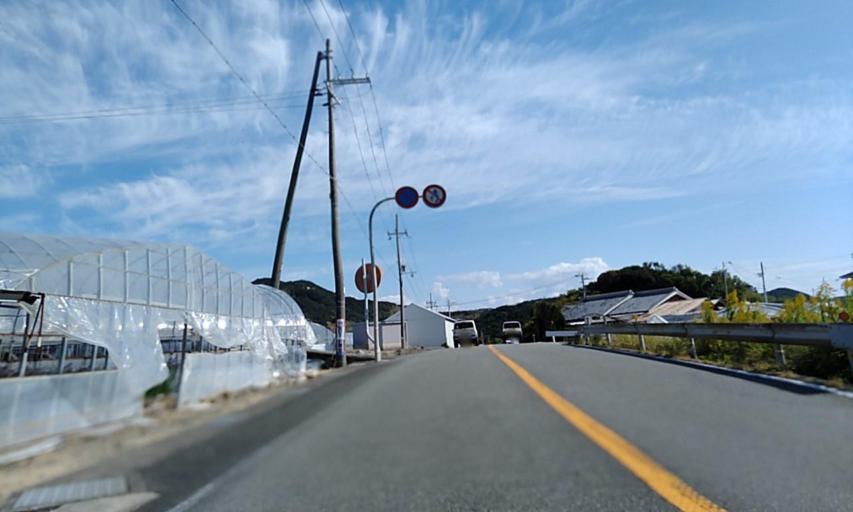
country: JP
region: Wakayama
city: Gobo
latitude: 33.8449
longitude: 135.1714
